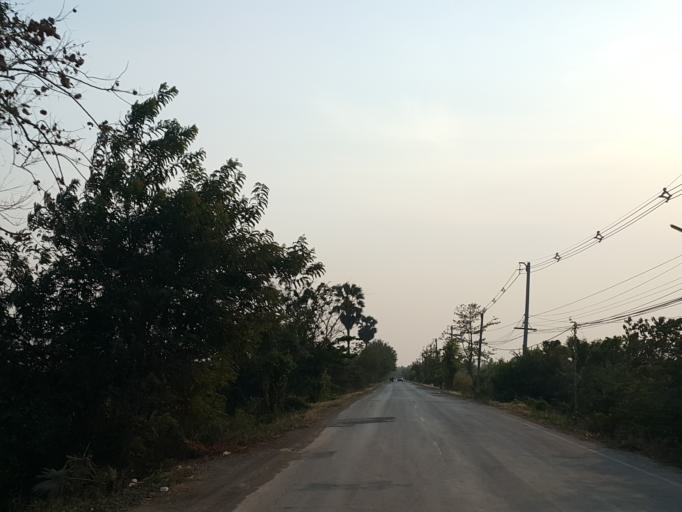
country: TH
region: Sukhothai
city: Si Samrong
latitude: 17.2158
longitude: 99.8827
